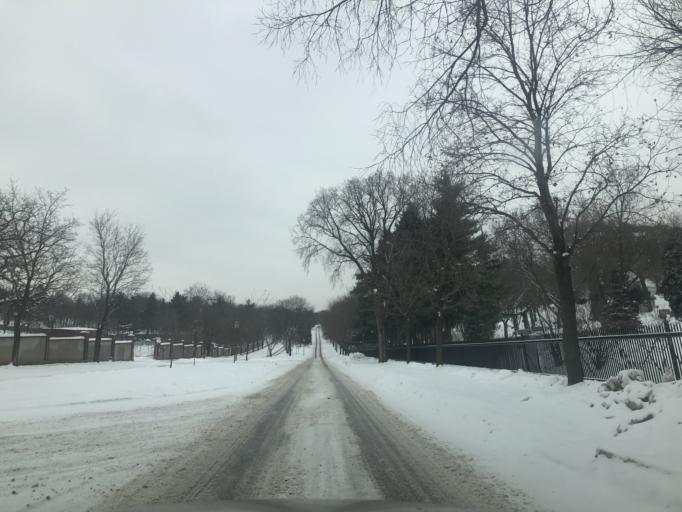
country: US
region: Minnesota
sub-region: Hennepin County
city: Richfield
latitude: 44.9337
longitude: -93.2935
